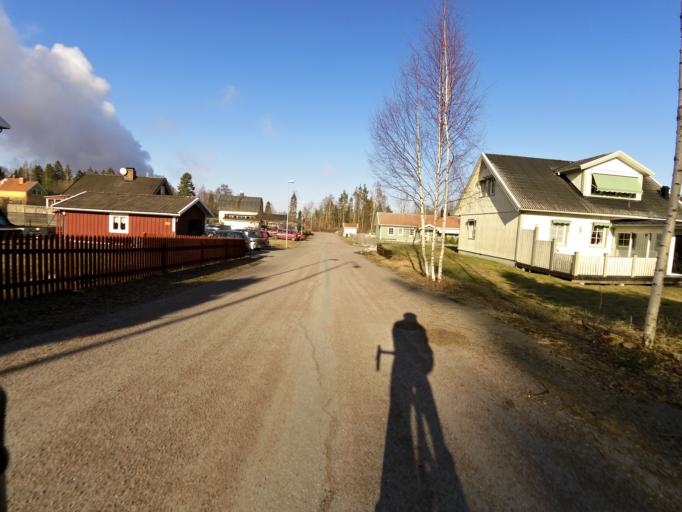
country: SE
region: Gaevleborg
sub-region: Gavle Kommun
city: Gavle
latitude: 60.6725
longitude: 17.2713
